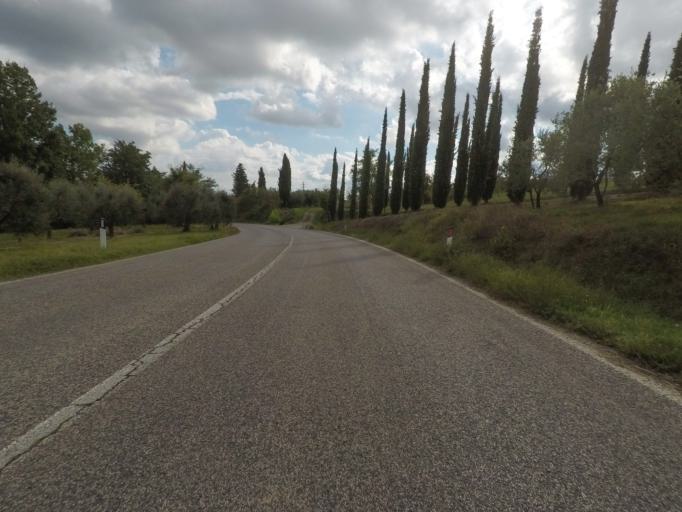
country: IT
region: Tuscany
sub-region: Provincia di Siena
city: Torrita di Siena
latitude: 43.1510
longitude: 11.7786
